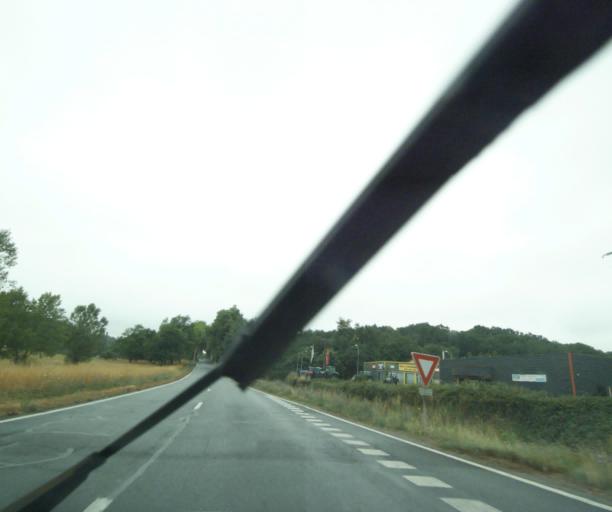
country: FR
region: Midi-Pyrenees
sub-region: Departement du Tarn
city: Arthes
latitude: 43.9717
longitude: 2.1828
